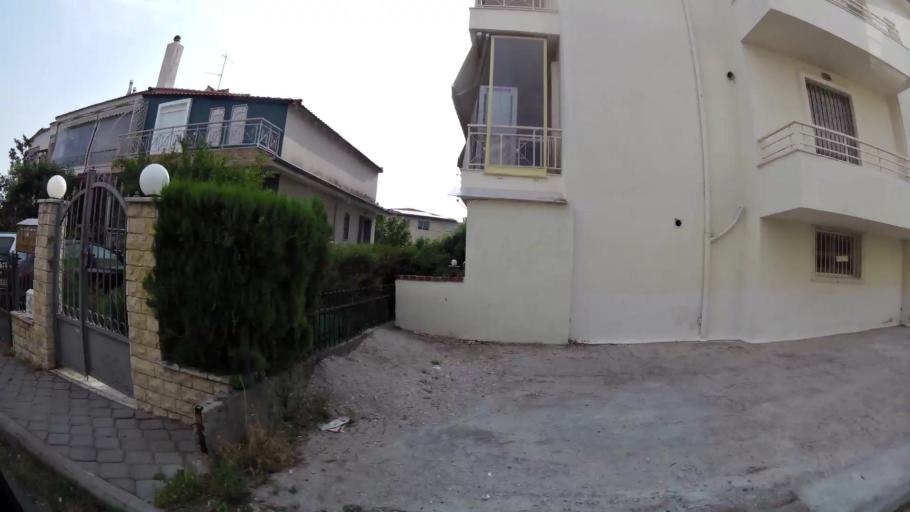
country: GR
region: Central Macedonia
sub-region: Nomos Thessalonikis
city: Oraiokastro
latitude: 40.7251
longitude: 22.9204
